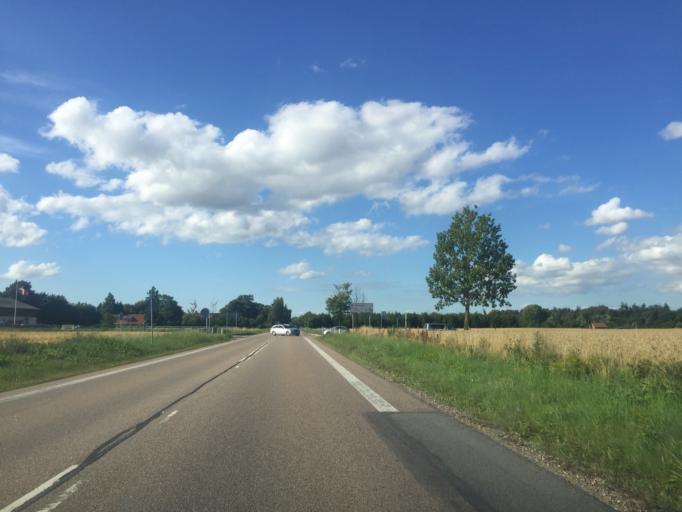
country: DK
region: Zealand
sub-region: Guldborgsund Kommune
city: Nykobing Falster
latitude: 54.6768
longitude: 11.9060
